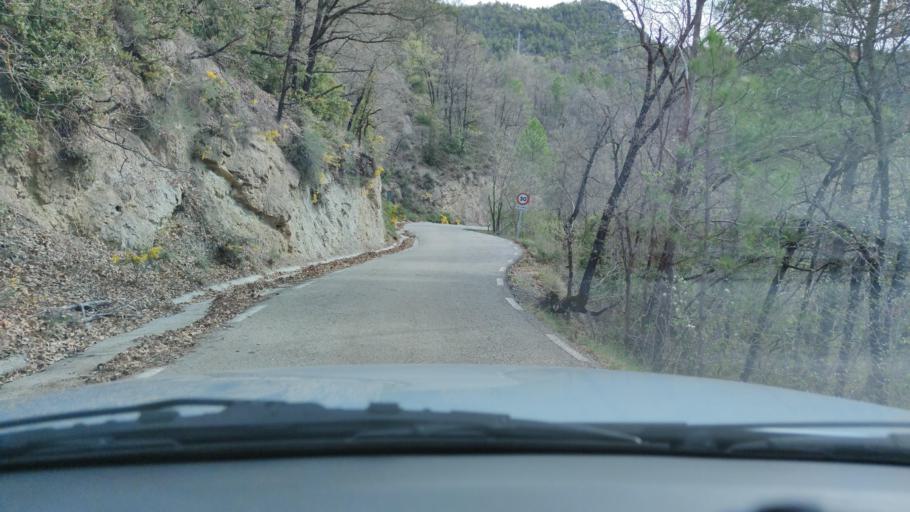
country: ES
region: Catalonia
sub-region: Provincia de Lleida
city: la Seu d'Urgell
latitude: 42.2397
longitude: 1.4328
